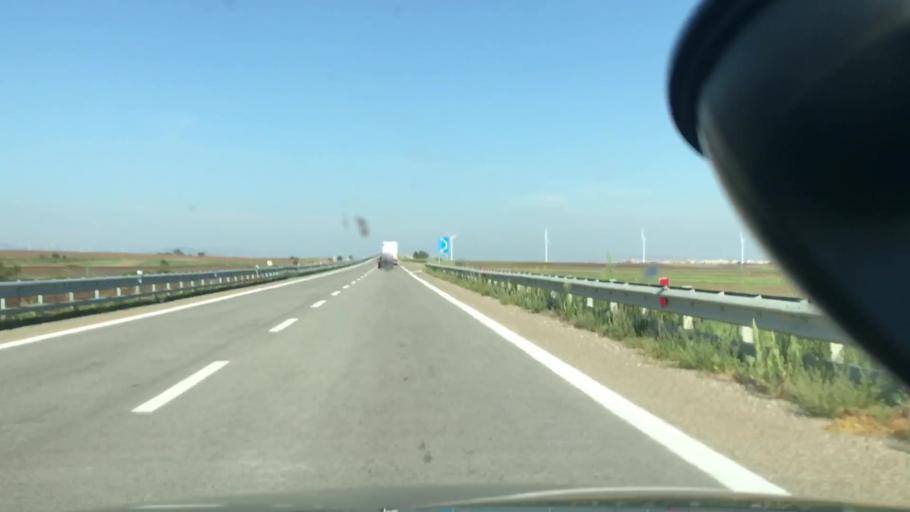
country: IT
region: Basilicate
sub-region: Provincia di Potenza
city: Venosa
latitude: 41.0119
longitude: 15.8322
